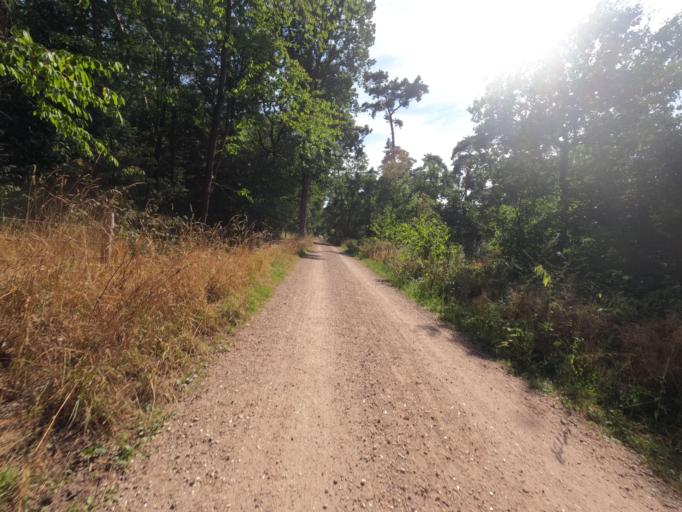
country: NL
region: Limburg
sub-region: Gemeente Beesel
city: Offenbeek
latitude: 51.2730
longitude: 6.1220
